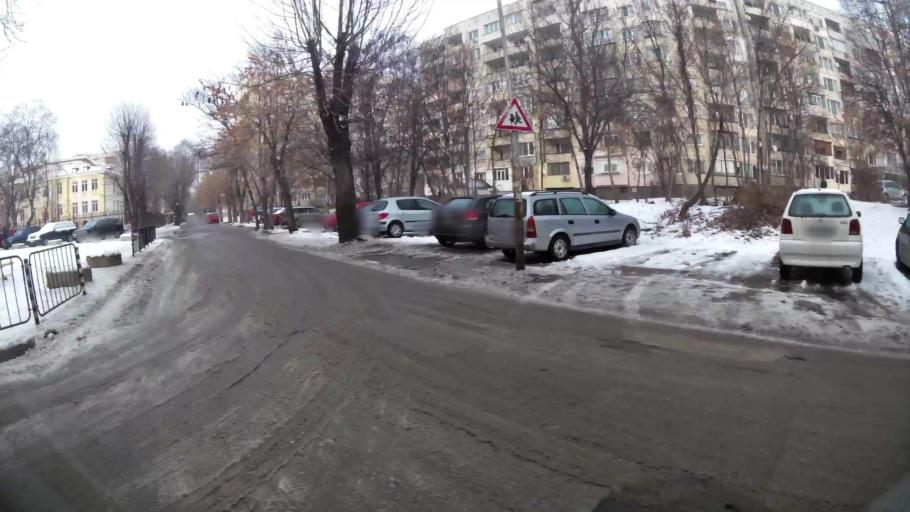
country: BG
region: Sofia-Capital
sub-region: Stolichna Obshtina
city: Sofia
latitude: 42.7110
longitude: 23.2989
